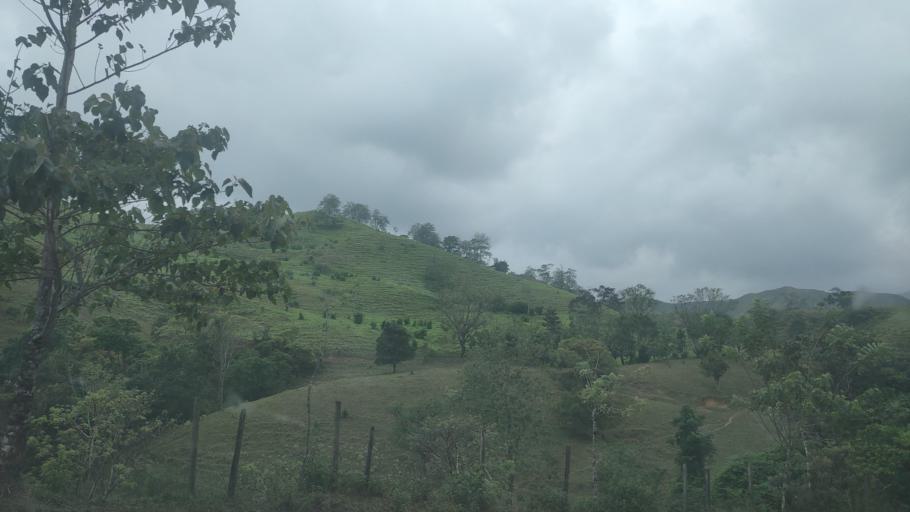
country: MX
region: Tabasco
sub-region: Huimanguillo
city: Francisco Rueda
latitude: 17.4390
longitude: -94.0300
